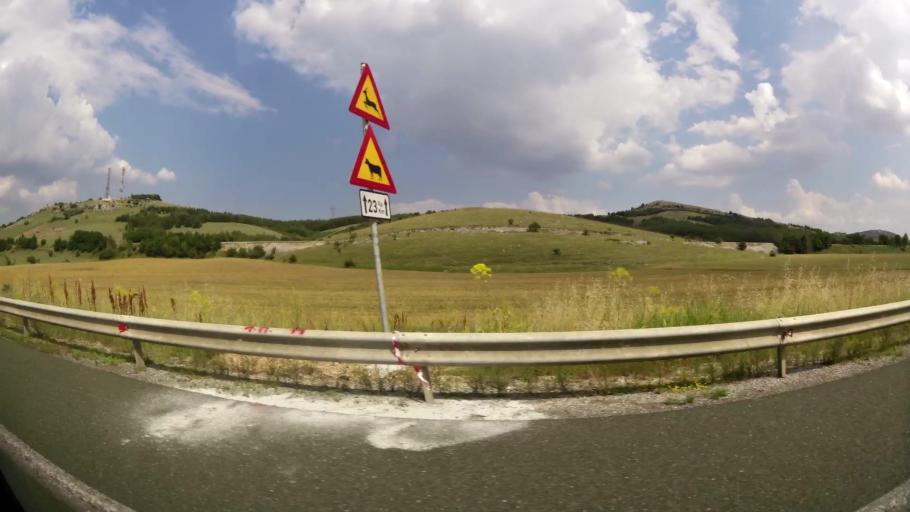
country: GR
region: West Macedonia
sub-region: Nomos Kozanis
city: Koila
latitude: 40.3547
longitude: 21.8123
